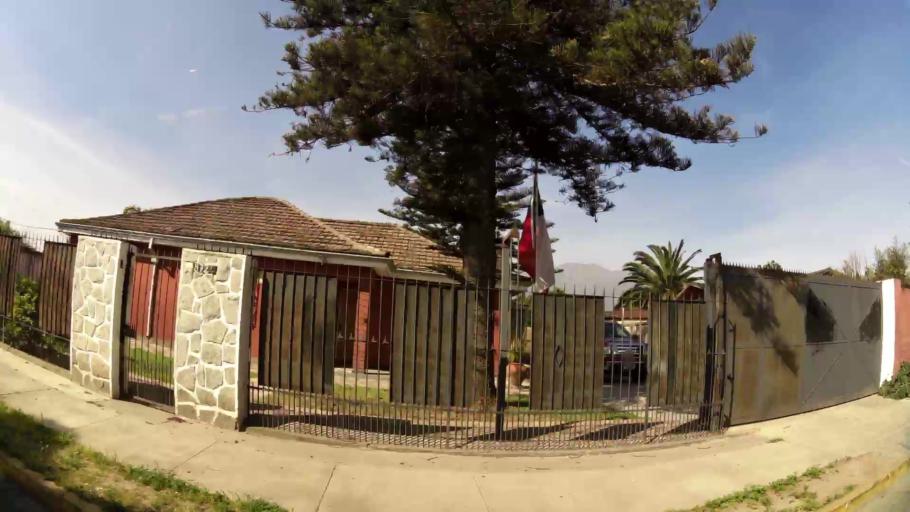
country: CL
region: Santiago Metropolitan
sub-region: Provincia de Santiago
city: La Pintana
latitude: -33.5350
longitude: -70.5917
